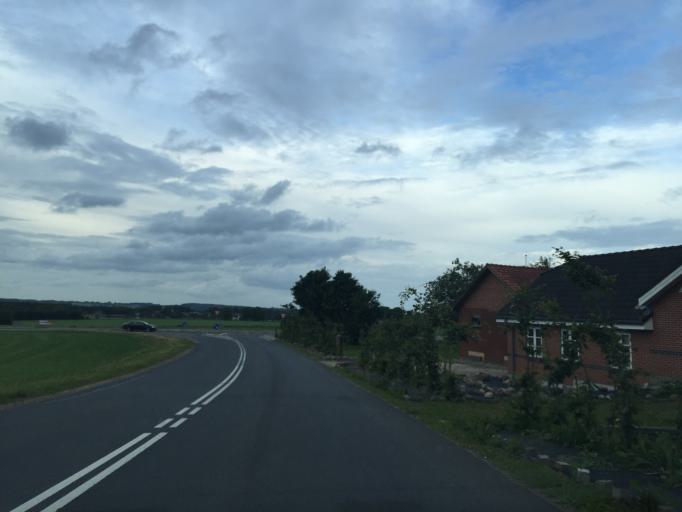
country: DK
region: Central Jutland
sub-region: Silkeborg Kommune
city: Kjellerup
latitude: 56.2345
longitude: 9.4754
